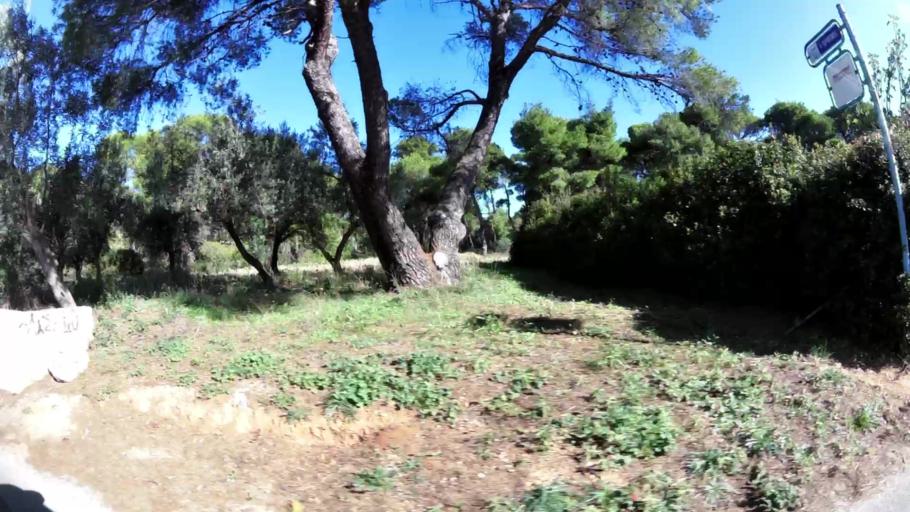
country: GR
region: Attica
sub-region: Nomarchia Anatolikis Attikis
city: Varybobi
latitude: 38.1306
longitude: 23.7919
